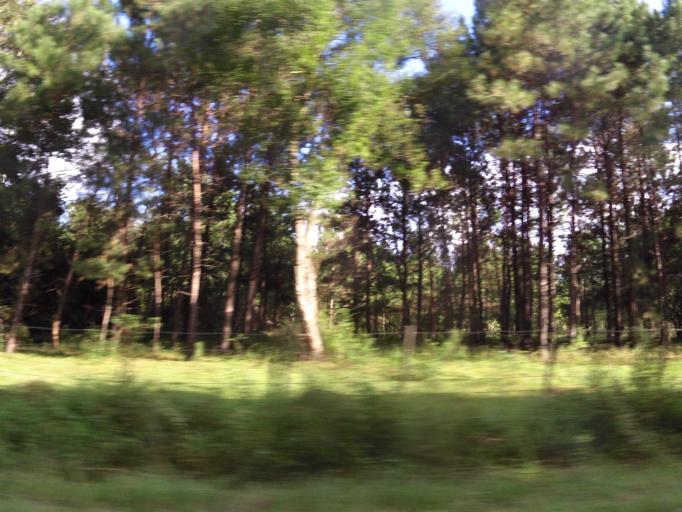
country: US
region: Georgia
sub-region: Brooks County
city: Quitman
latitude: 30.7817
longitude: -83.5905
